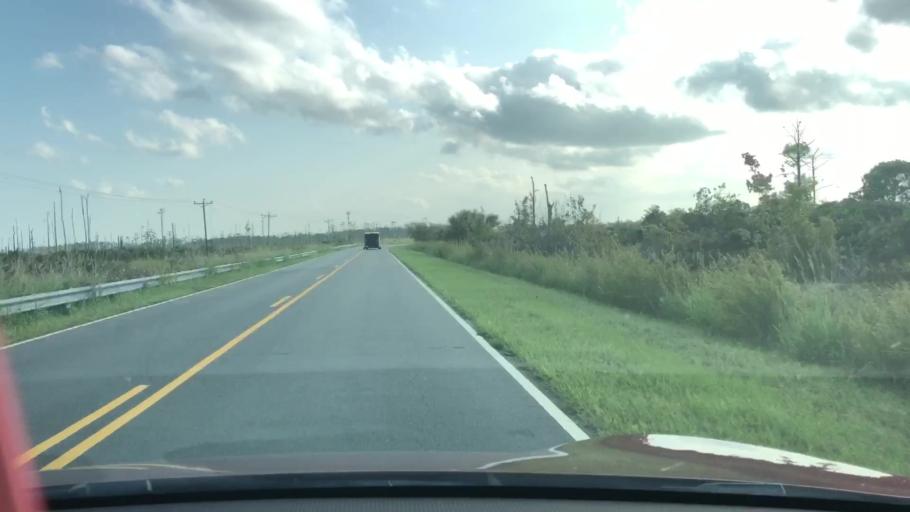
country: US
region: North Carolina
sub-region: Dare County
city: Wanchese
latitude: 35.6232
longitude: -75.7863
